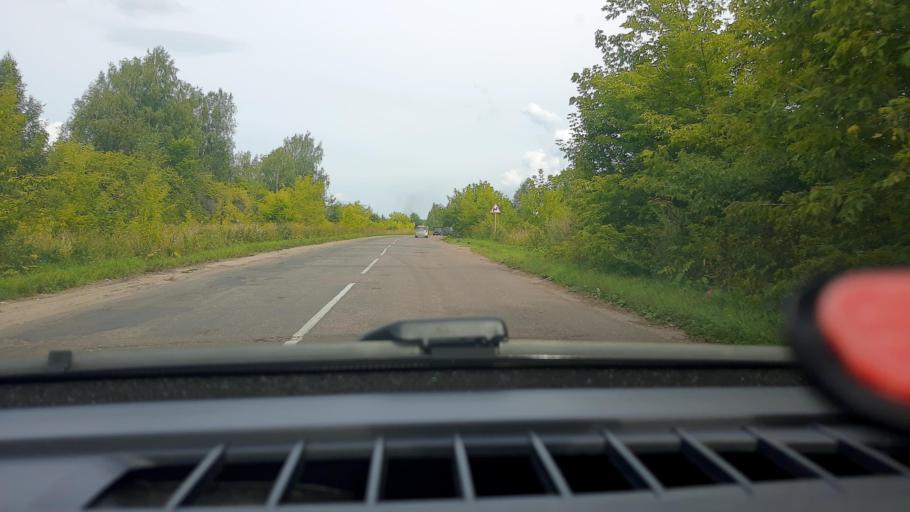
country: RU
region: Nizjnij Novgorod
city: Bogorodsk
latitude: 56.0738
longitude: 43.5768
